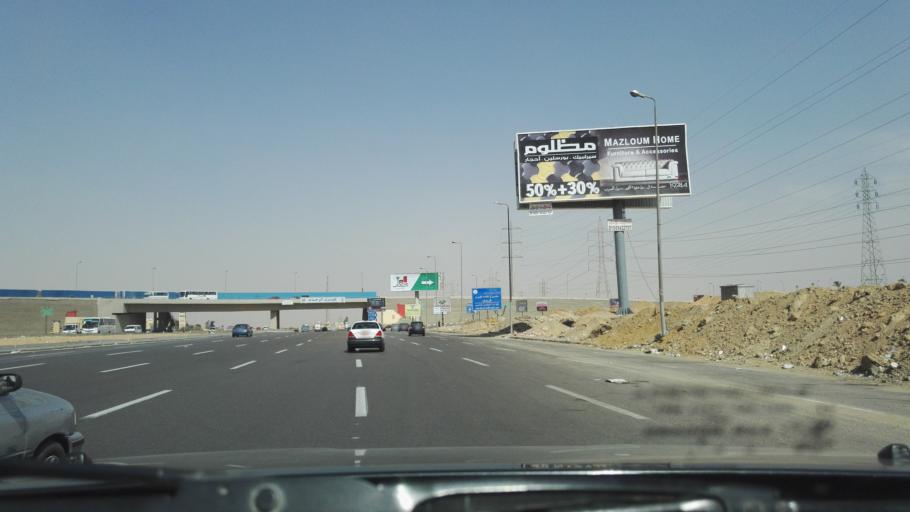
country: EG
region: Muhafazat al Qalyubiyah
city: Al Khankah
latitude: 30.0826
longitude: 31.4682
